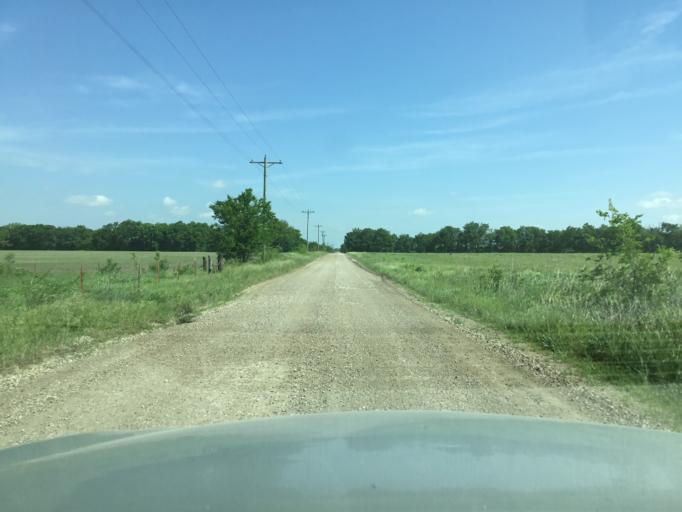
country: US
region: Kansas
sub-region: Labette County
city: Oswego
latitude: 37.1681
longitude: -95.1399
